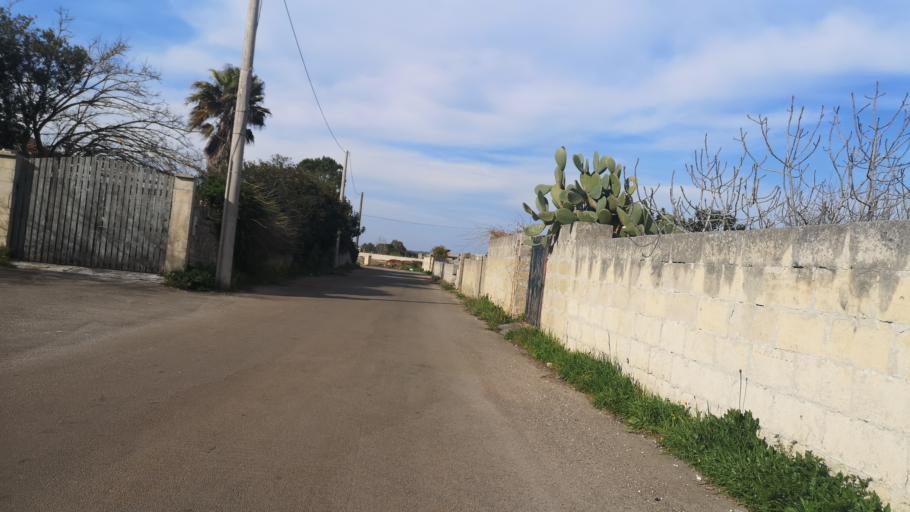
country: IT
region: Apulia
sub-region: Provincia di Lecce
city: Spongano
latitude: 40.0207
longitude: 18.3697
